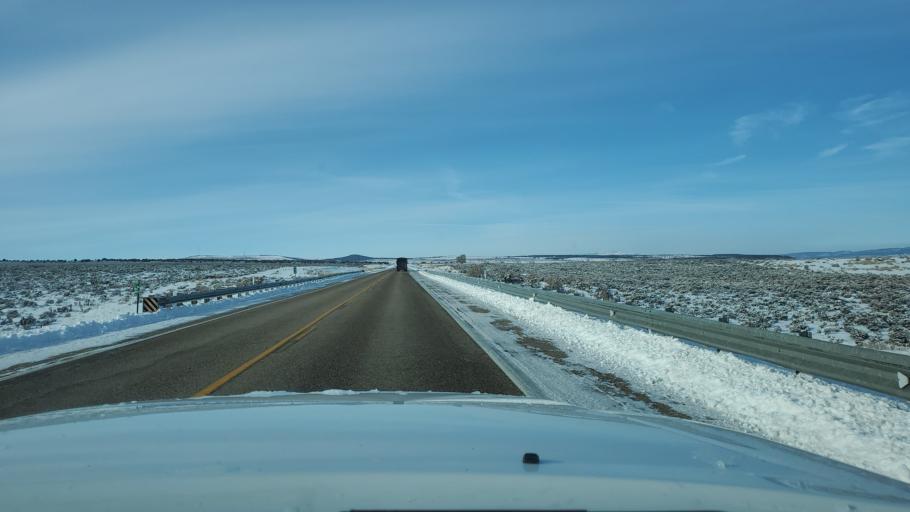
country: US
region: Colorado
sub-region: Rio Blanco County
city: Meeker
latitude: 40.4200
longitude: -108.3145
